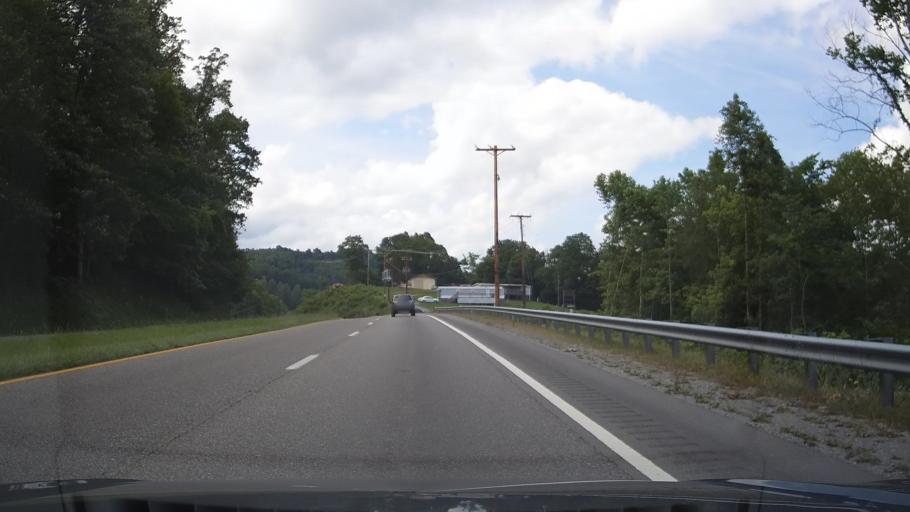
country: US
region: Tennessee
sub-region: Hawkins County
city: Mount Carmel
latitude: 36.6915
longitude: -82.7533
